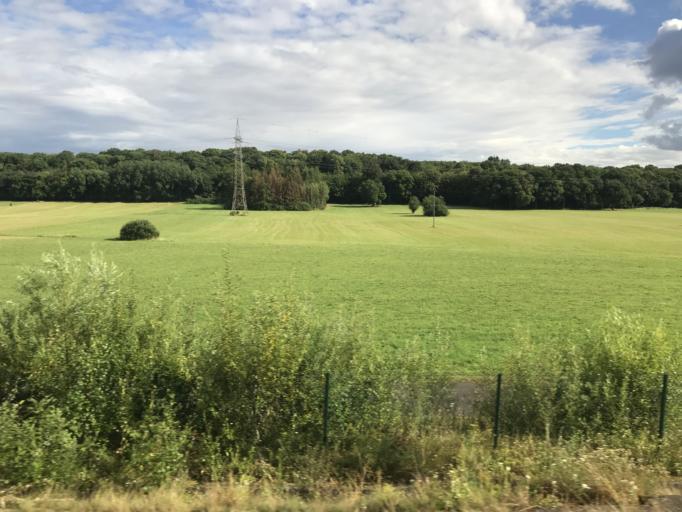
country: LU
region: Luxembourg
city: Schouweiler
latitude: 49.5717
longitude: 5.9491
